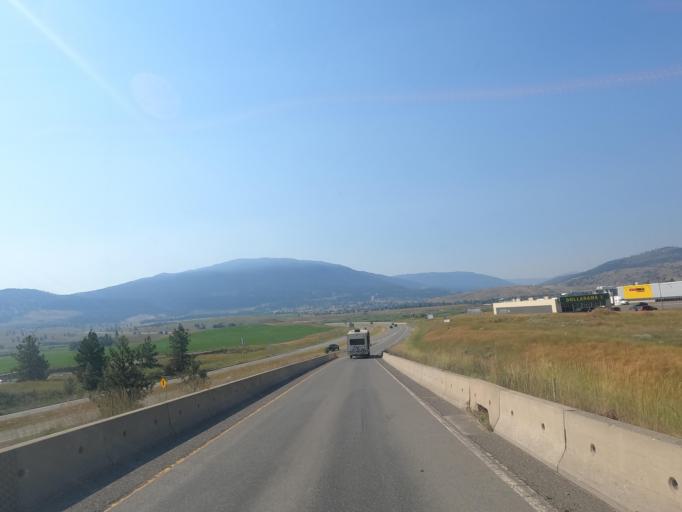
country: CA
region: British Columbia
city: Merritt
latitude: 50.1220
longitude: -120.7596
